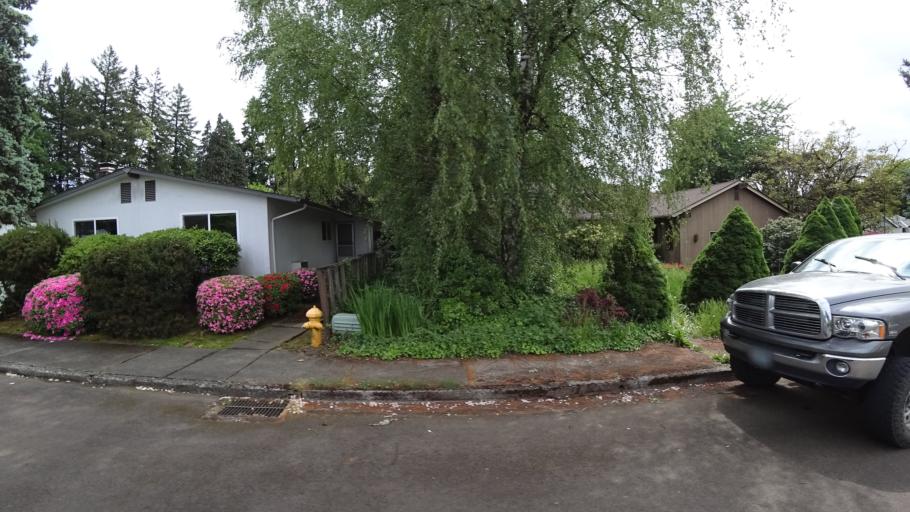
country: US
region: Oregon
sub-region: Washington County
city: Raleigh Hills
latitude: 45.4781
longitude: -122.7651
